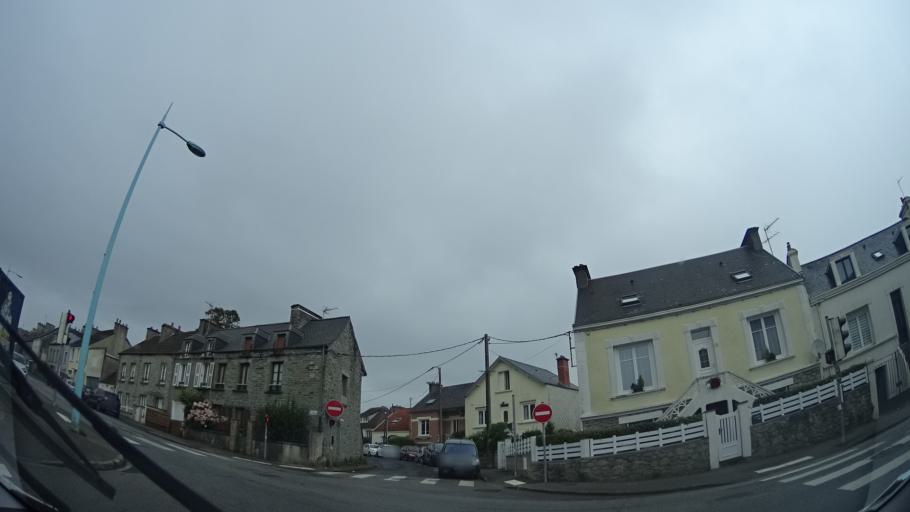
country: FR
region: Lower Normandy
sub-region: Departement de la Manche
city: Octeville
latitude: 49.6321
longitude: -1.6379
